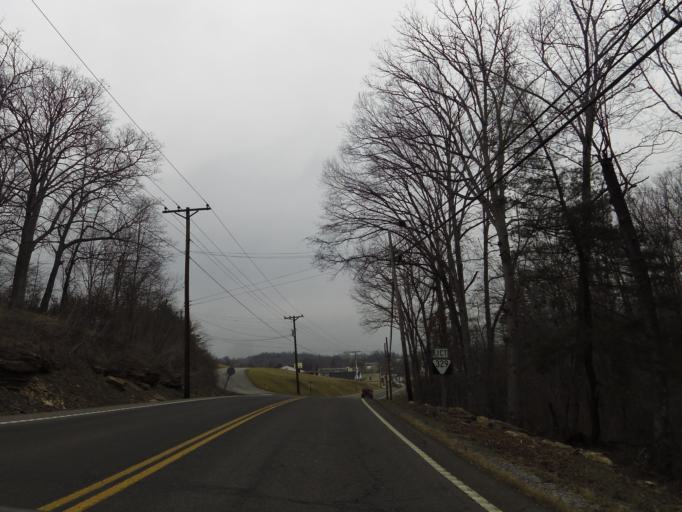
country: US
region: Tennessee
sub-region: Morgan County
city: Wartburg
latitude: 36.2403
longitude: -84.6712
